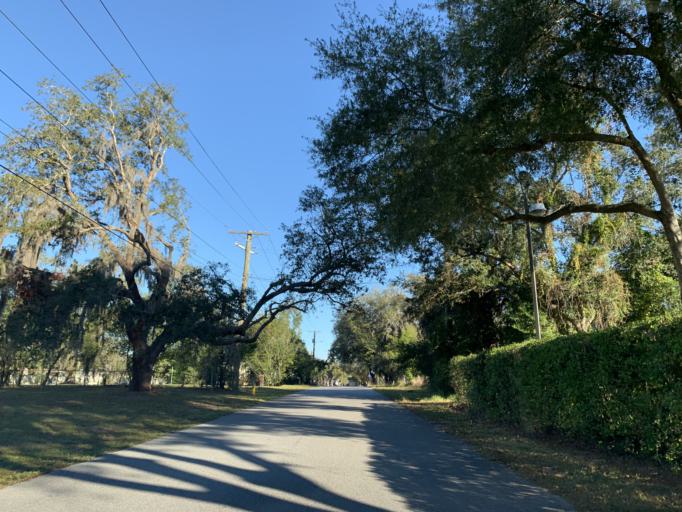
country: US
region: Florida
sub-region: Hillsborough County
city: University
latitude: 28.0341
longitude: -82.4274
